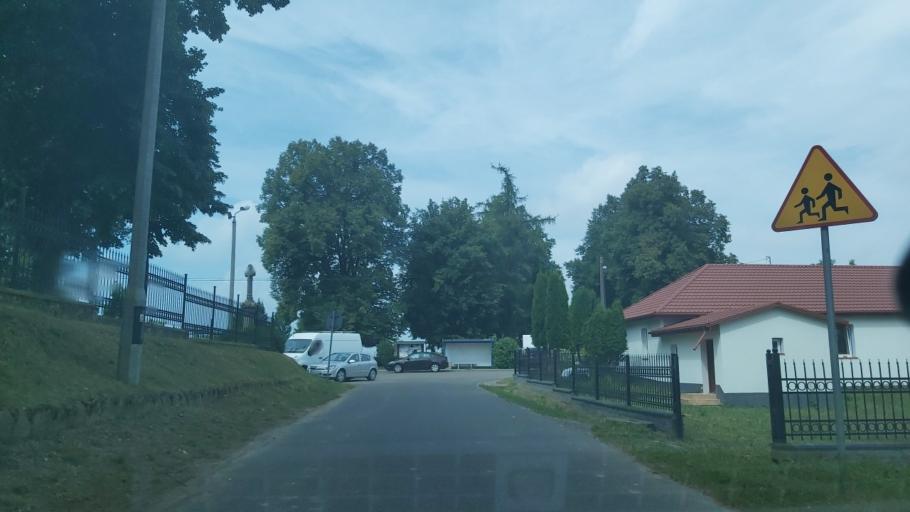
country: PL
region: Kujawsko-Pomorskie
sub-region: Powiat golubsko-dobrzynski
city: Zbojno
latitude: 53.0320
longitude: 19.1697
